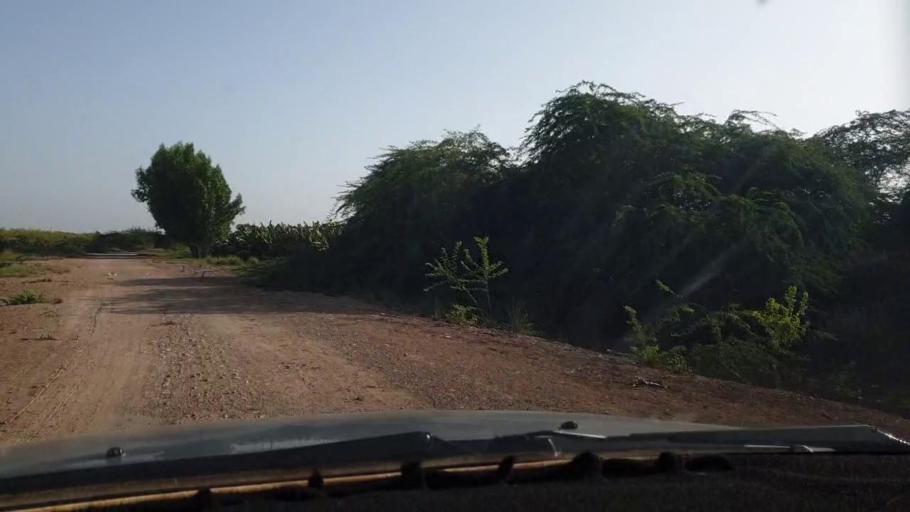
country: PK
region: Sindh
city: Mirwah Gorchani
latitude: 25.2942
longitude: 68.9333
